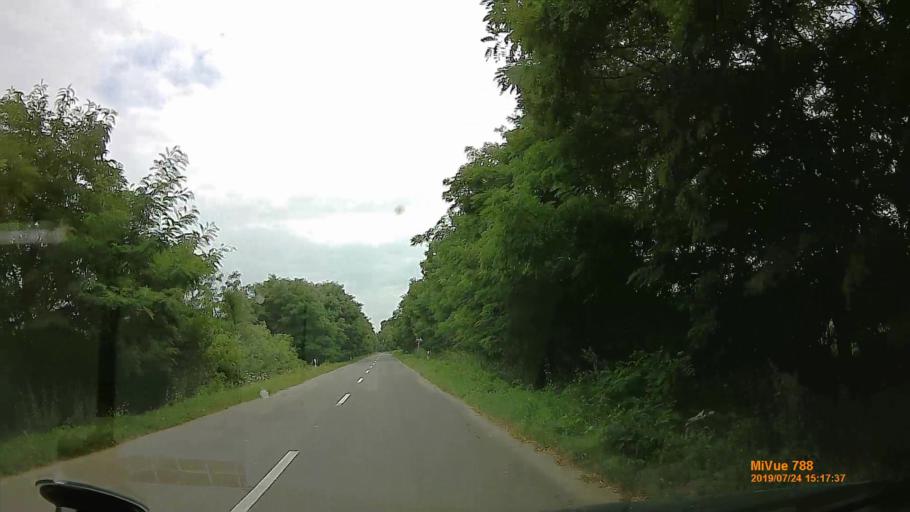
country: HU
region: Szabolcs-Szatmar-Bereg
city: Tarpa
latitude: 48.1905
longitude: 22.5480
